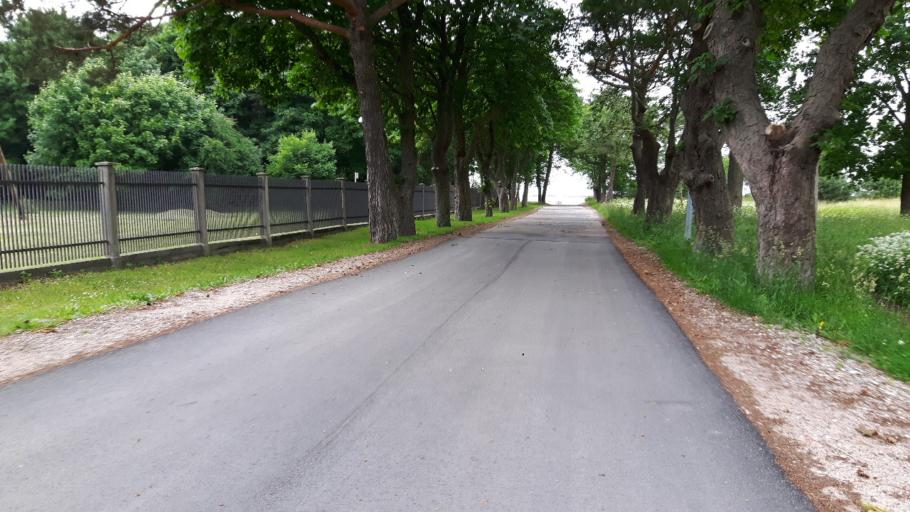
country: LV
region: Liepaja
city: Vec-Liepaja
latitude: 56.5533
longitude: 21.0036
